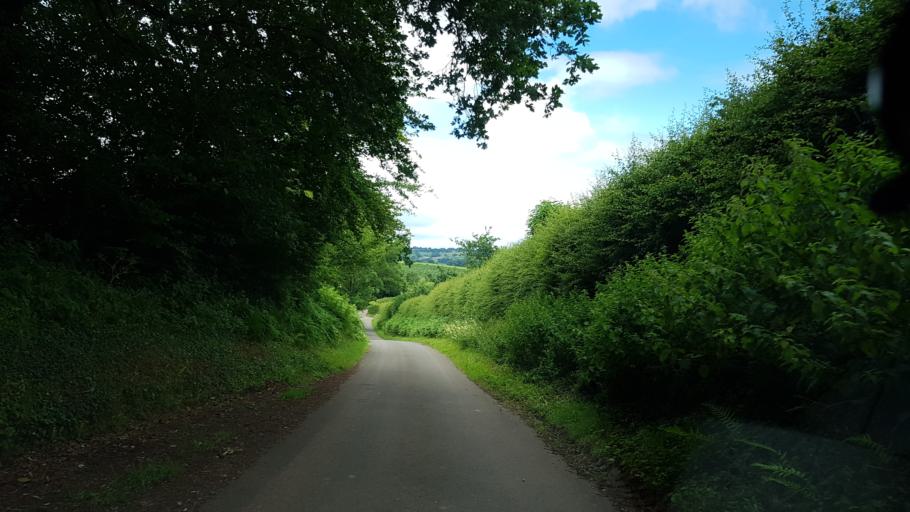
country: GB
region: Wales
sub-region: Monmouthshire
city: Llanarth
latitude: 51.8173
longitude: -2.8570
